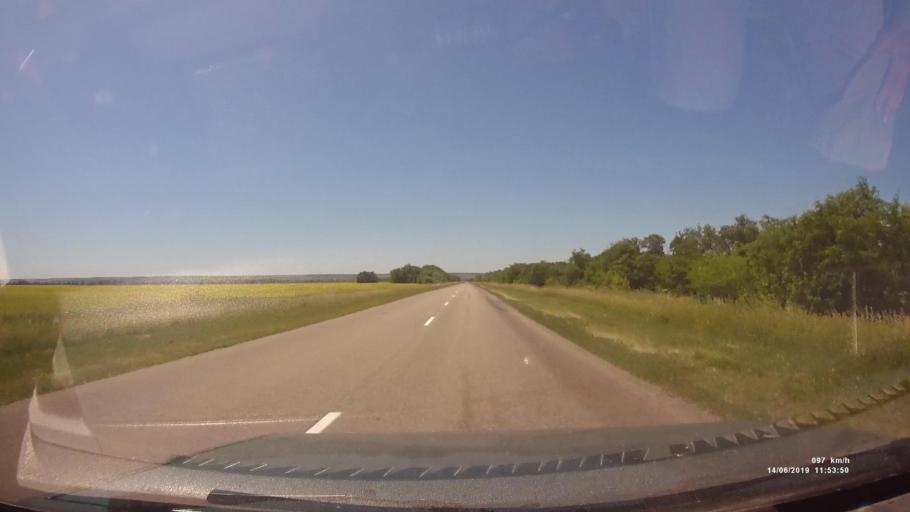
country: RU
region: Rostov
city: Kazanskaya
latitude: 49.8241
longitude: 41.2059
